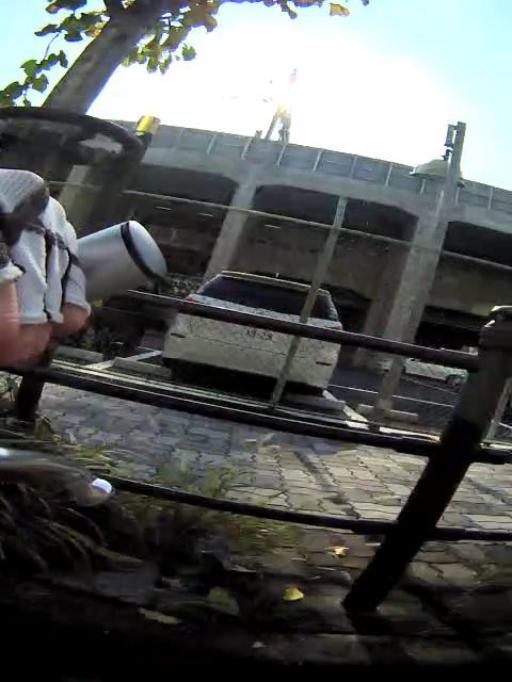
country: JP
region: Osaka
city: Suita
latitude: 34.7328
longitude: 135.4957
